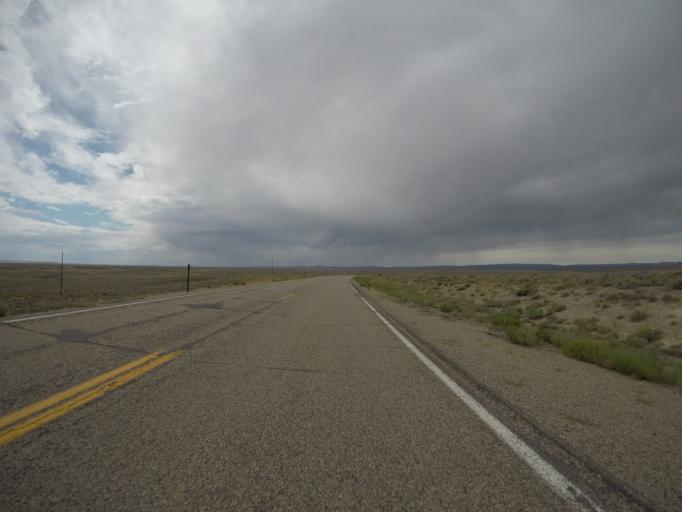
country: US
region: Wyoming
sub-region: Lincoln County
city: Kemmerer
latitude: 41.9626
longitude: -110.1014
